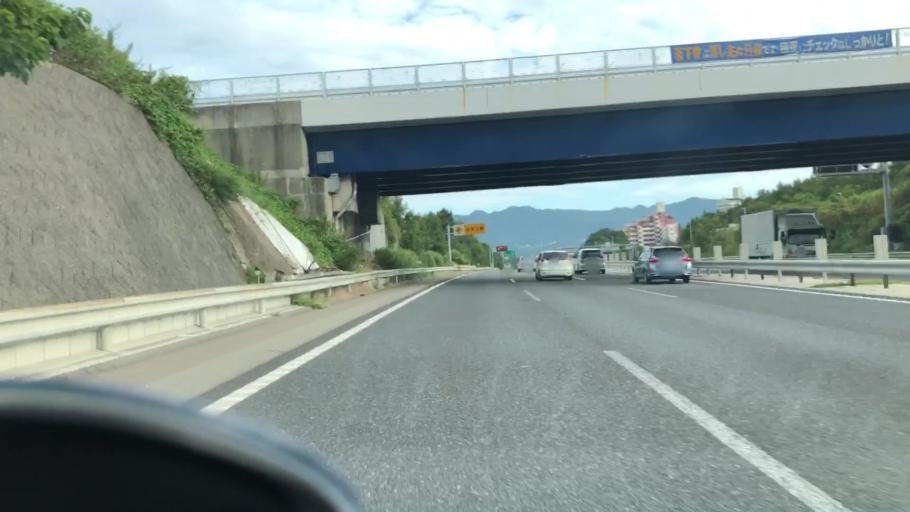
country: JP
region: Hyogo
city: Sandacho
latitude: 34.8483
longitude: 135.2239
